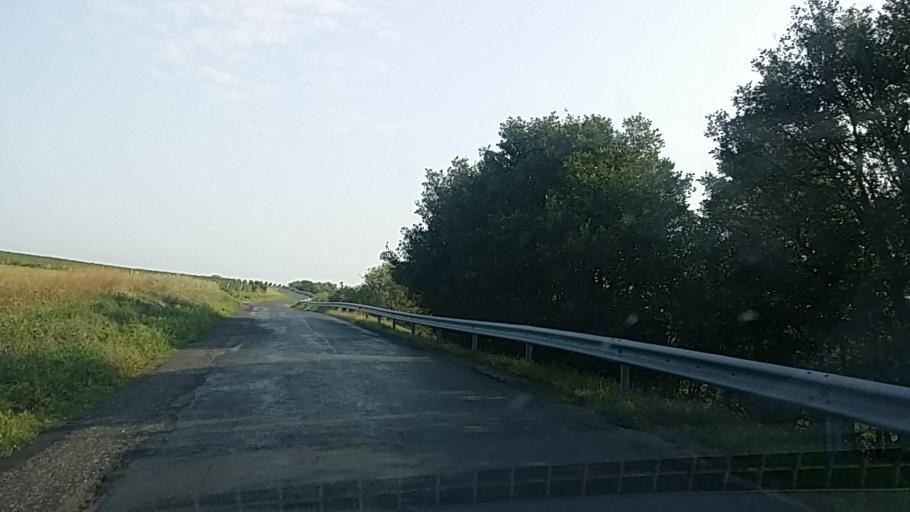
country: HU
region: Gyor-Moson-Sopron
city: Fertorakos
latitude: 47.6720
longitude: 16.6723
